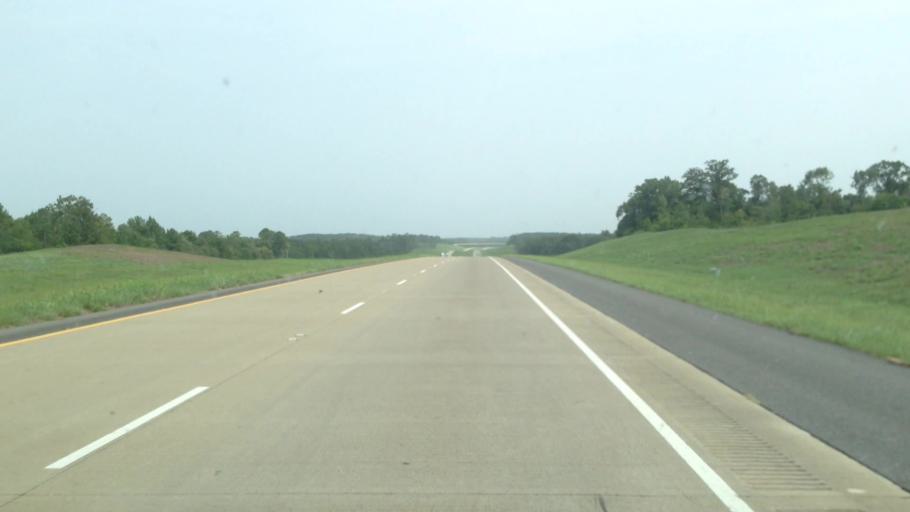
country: US
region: Louisiana
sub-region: Caddo Parish
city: Vivian
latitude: 32.9590
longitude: -93.9021
